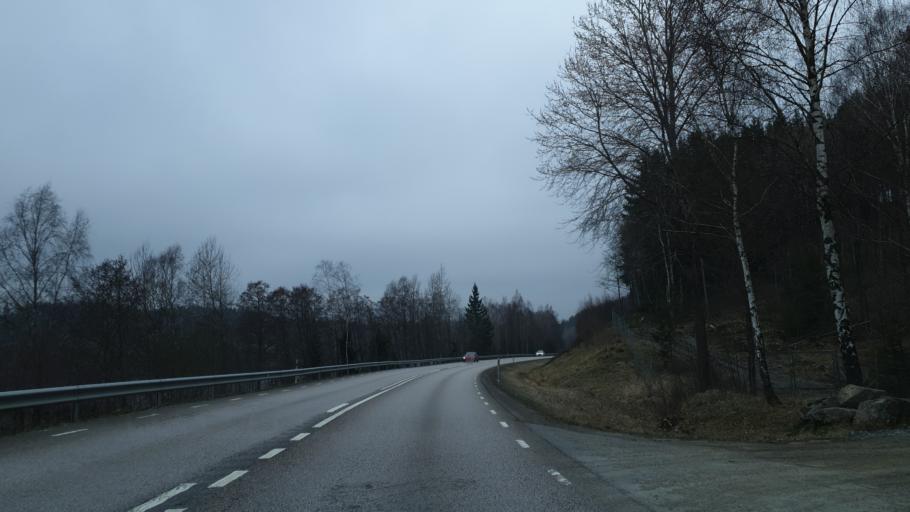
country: SE
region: Vaestra Goetaland
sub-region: Harryda Kommun
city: Hindas
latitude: 57.6266
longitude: 12.4141
